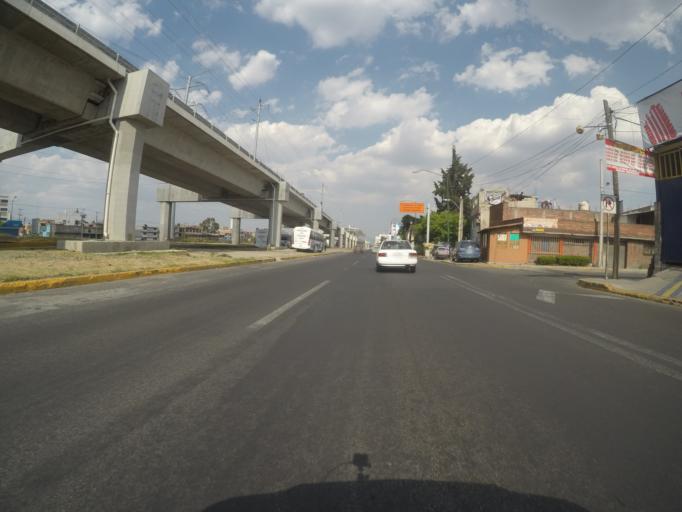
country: MX
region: Mexico
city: Toluca
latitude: 19.2693
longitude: -99.6449
